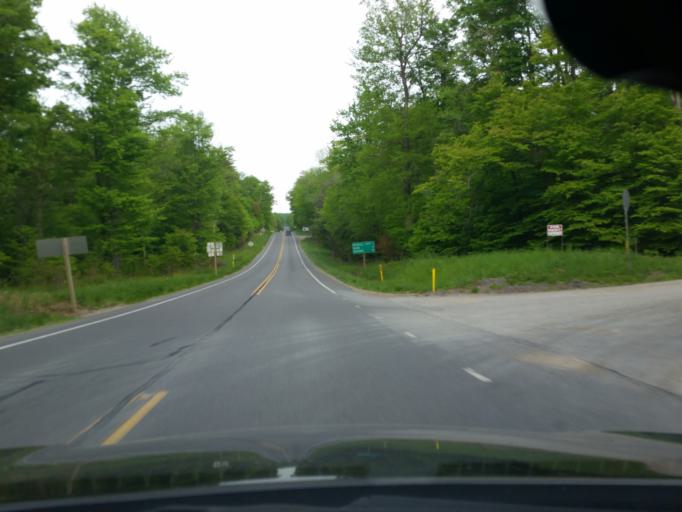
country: US
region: Pennsylvania
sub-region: McKean County
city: Kane
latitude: 41.5793
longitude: -78.9302
